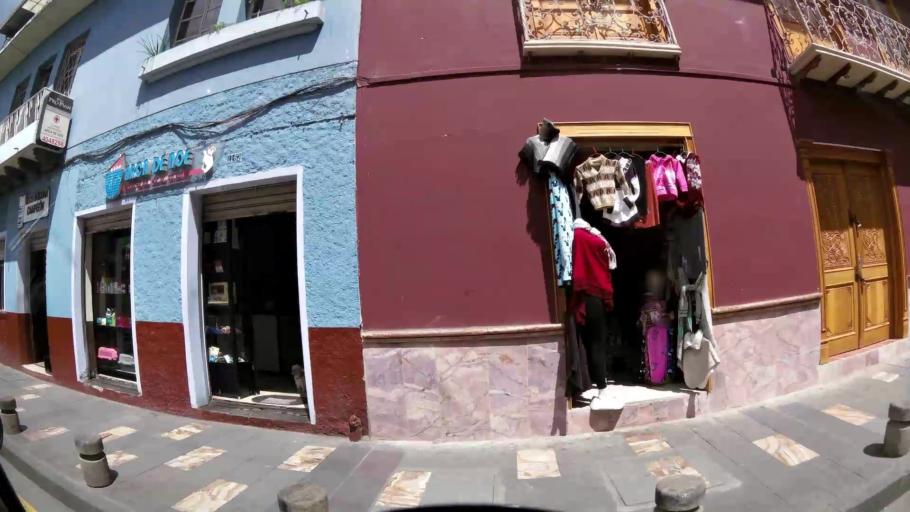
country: EC
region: Azuay
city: Cuenca
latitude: -2.8955
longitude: -78.9996
